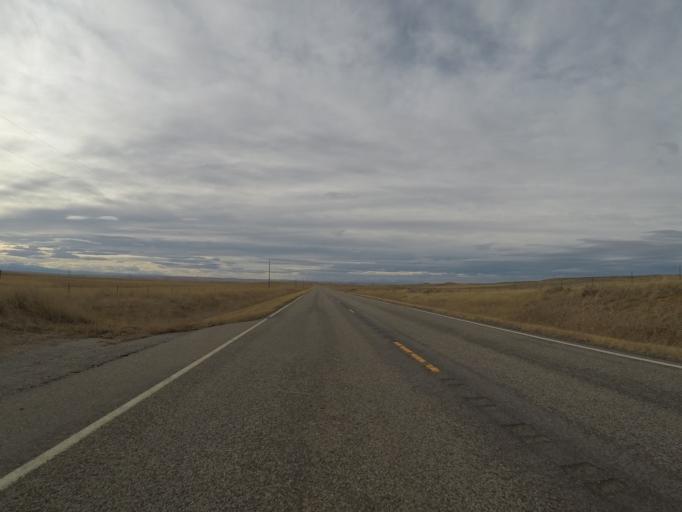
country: US
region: Montana
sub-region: Yellowstone County
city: Laurel
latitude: 45.8566
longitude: -108.8499
